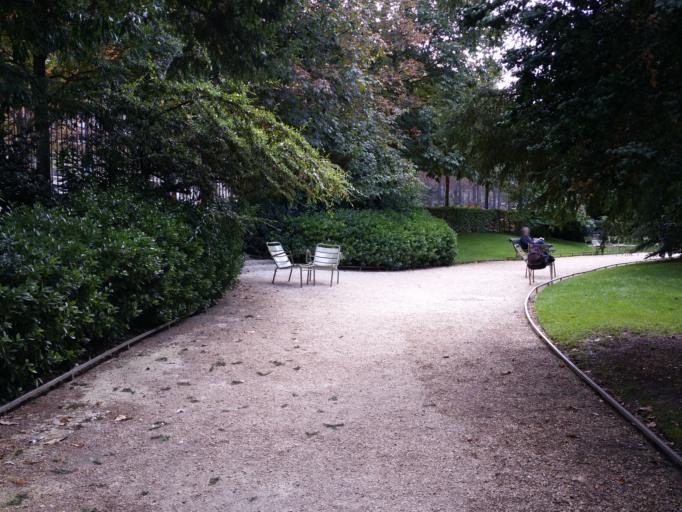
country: FR
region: Ile-de-France
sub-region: Paris
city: Paris
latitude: 48.8487
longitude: 2.3387
